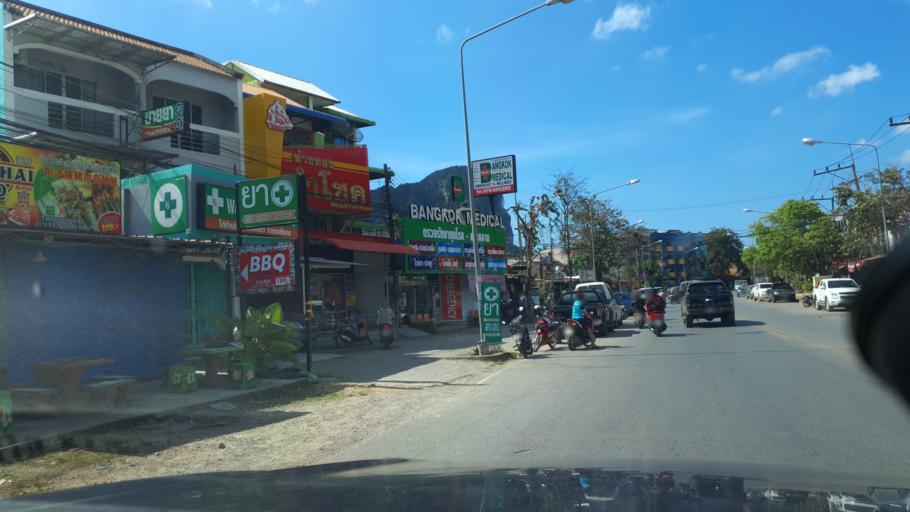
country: TH
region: Phangnga
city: Ban Ao Nang
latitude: 8.0401
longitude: 98.8358
